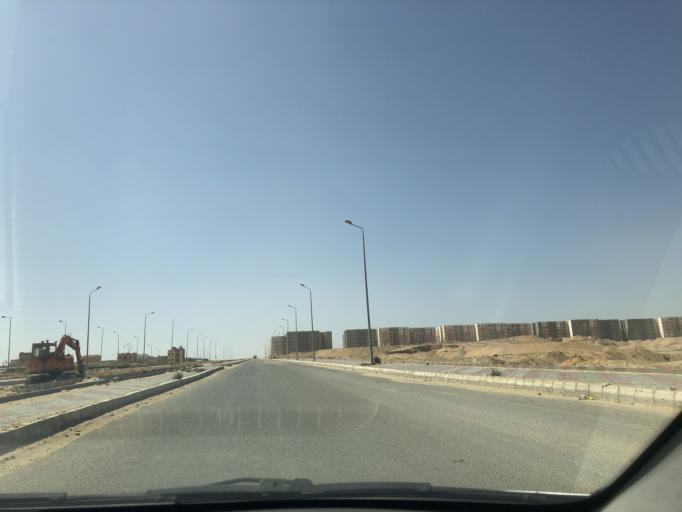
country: EG
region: Al Jizah
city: Madinat Sittah Uktubar
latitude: 29.9313
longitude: 31.0115
